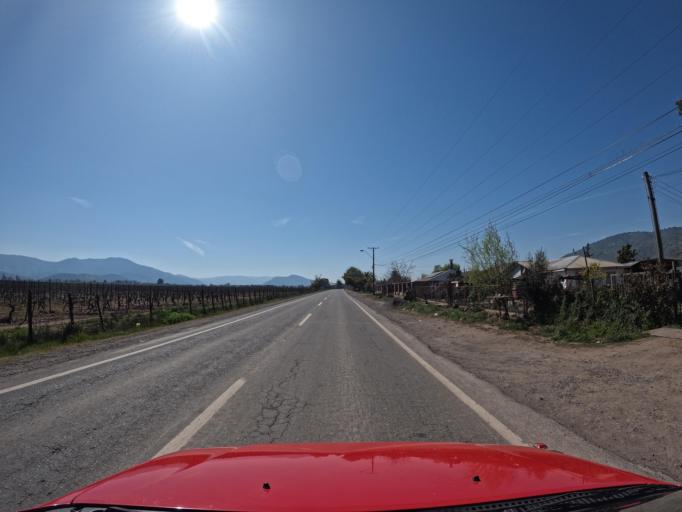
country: CL
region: Maule
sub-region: Provincia de Curico
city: Rauco
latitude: -35.0192
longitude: -71.4271
